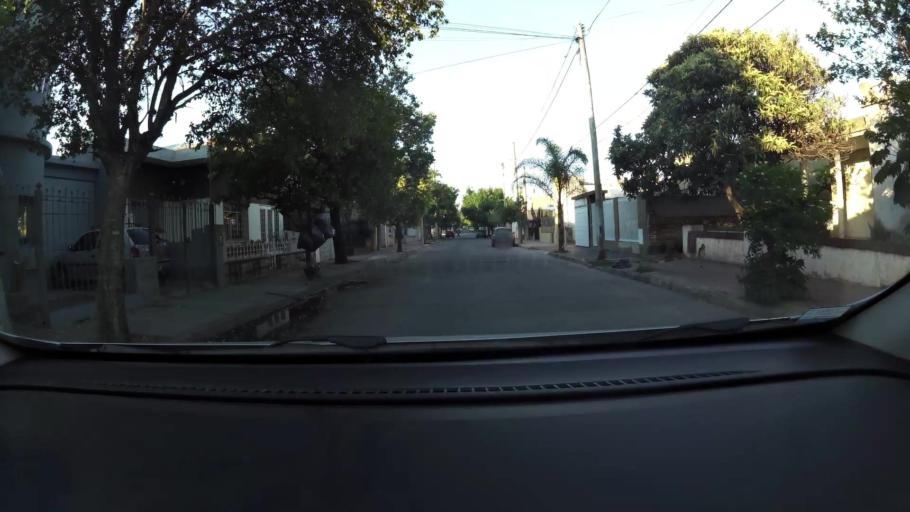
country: AR
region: Cordoba
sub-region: Departamento de Capital
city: Cordoba
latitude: -31.3892
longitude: -64.2117
